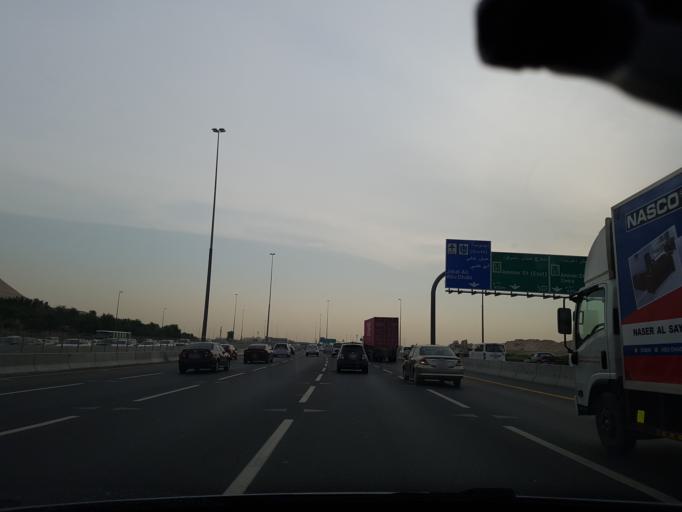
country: AE
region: Ash Shariqah
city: Sharjah
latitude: 25.2850
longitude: 55.4258
